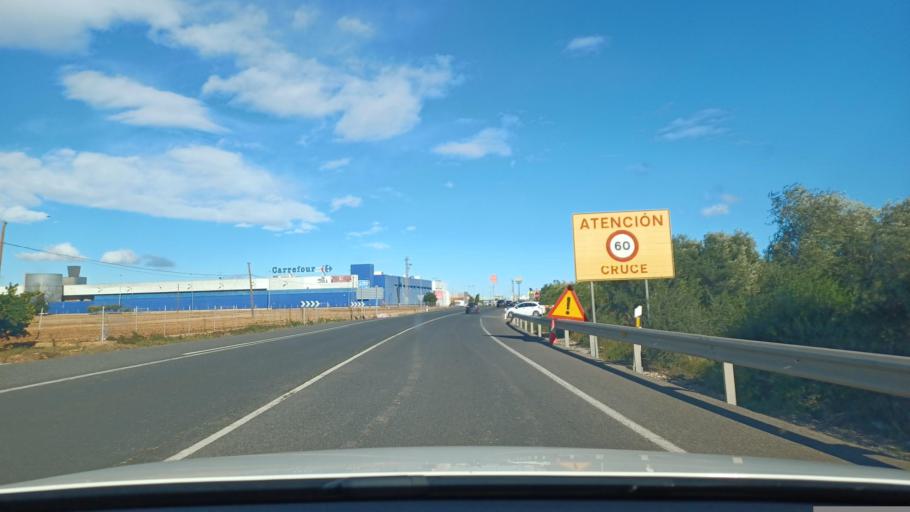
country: ES
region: Valencia
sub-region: Provincia de Castello
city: Vinaros
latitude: 40.4516
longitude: 0.4509
